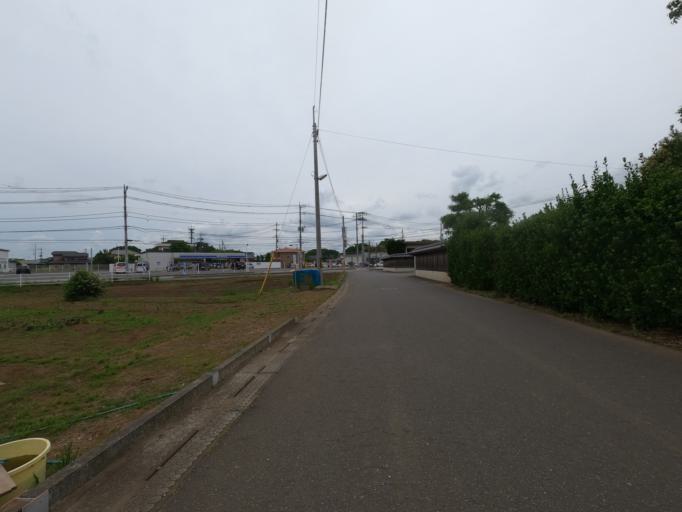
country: JP
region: Ibaraki
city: Moriya
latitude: 35.9447
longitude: 139.9691
